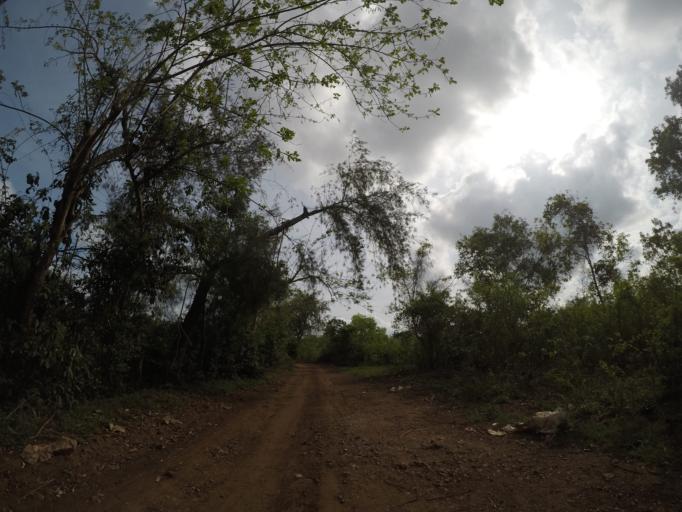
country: TZ
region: Zanzibar Central/South
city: Koani
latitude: -6.2208
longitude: 39.3198
